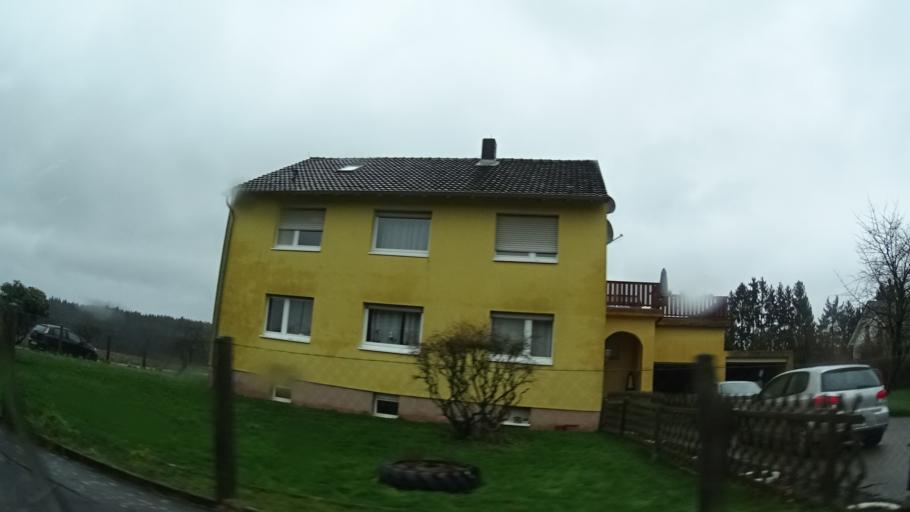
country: DE
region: Hesse
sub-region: Regierungsbezirk Kassel
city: Dipperz
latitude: 50.5626
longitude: 9.7840
